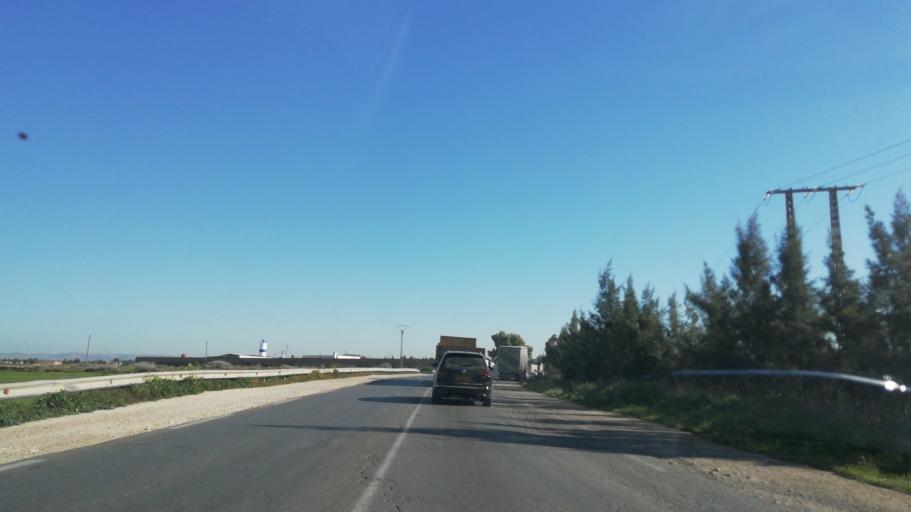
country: DZ
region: Relizane
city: Zemoura
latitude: 35.7547
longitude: 0.6800
